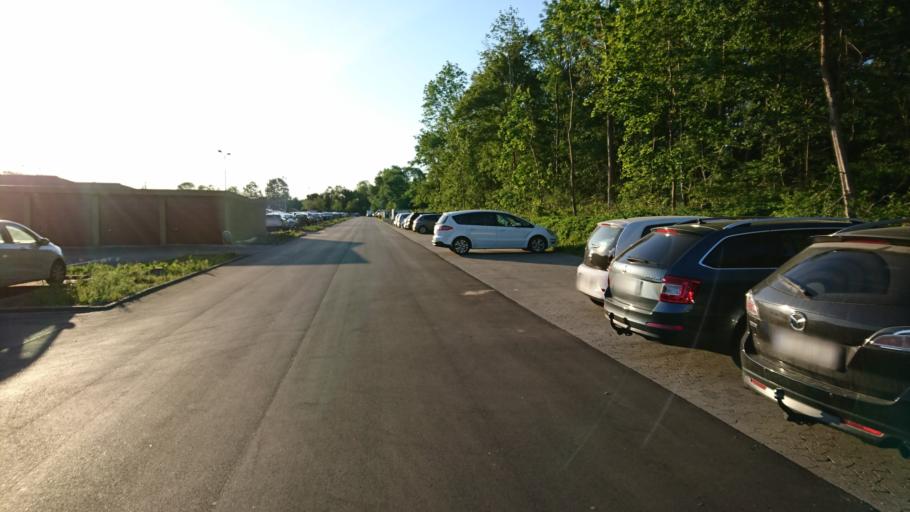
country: DK
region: Capital Region
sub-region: Ballerup Kommune
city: Ballerup
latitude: 55.7236
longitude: 12.3368
